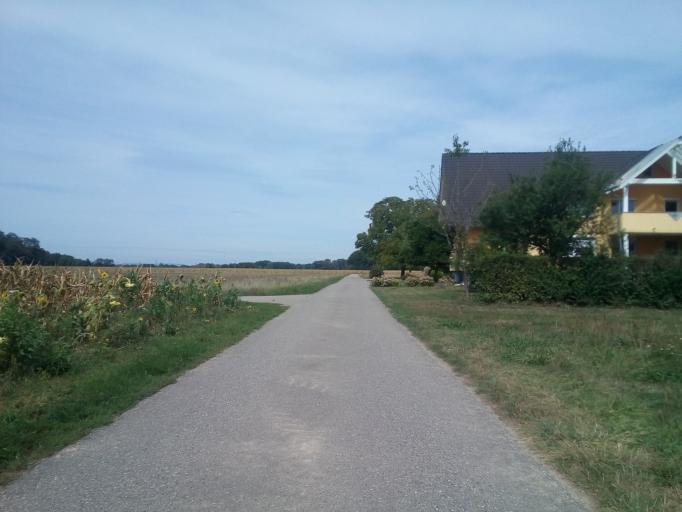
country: DE
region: Baden-Wuerttemberg
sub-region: Karlsruhe Region
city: Zell
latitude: 48.7013
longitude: 8.0459
